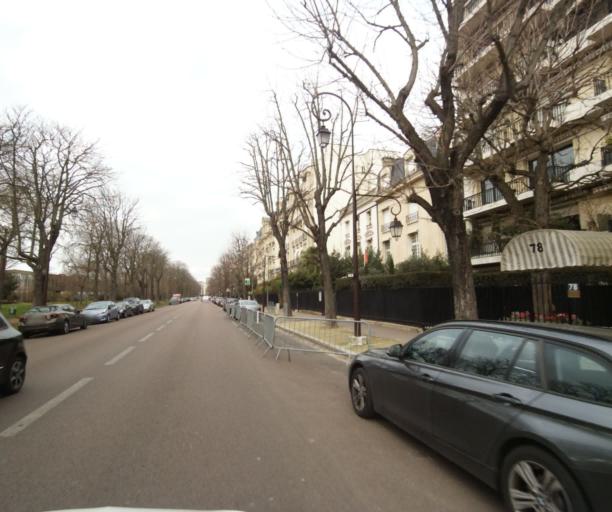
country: FR
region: Ile-de-France
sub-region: Departement des Hauts-de-Seine
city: Neuilly-sur-Seine
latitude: 48.8795
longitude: 2.2664
